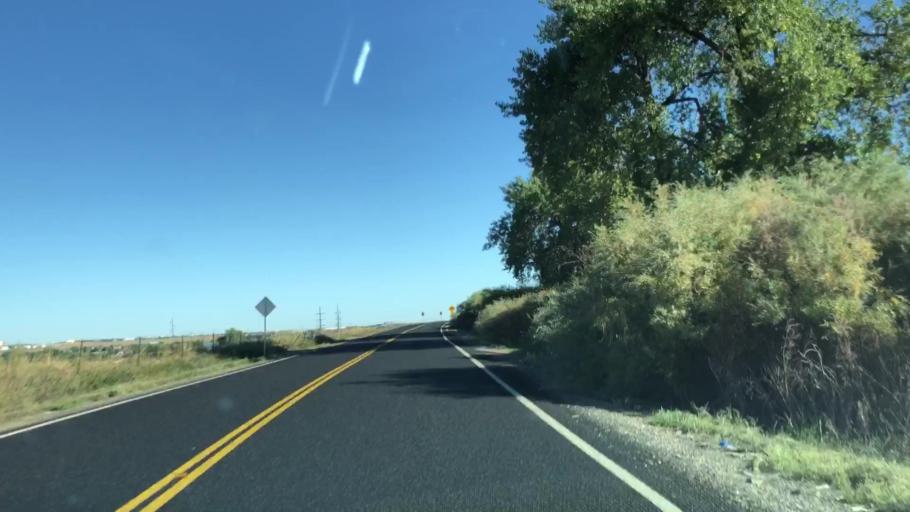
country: US
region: Colorado
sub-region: Larimer County
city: Loveland
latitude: 40.4631
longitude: -105.0508
